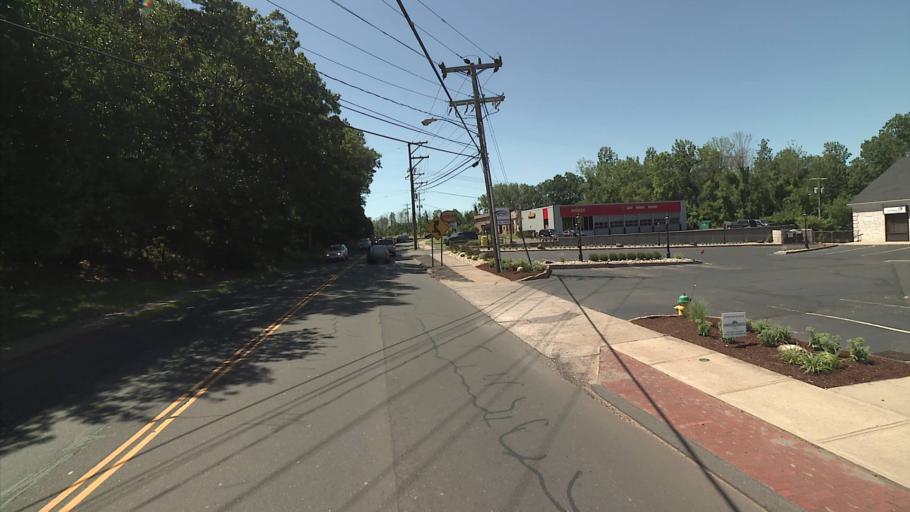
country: US
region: Connecticut
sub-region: Hartford County
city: Plainville
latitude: 41.6199
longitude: -72.8736
